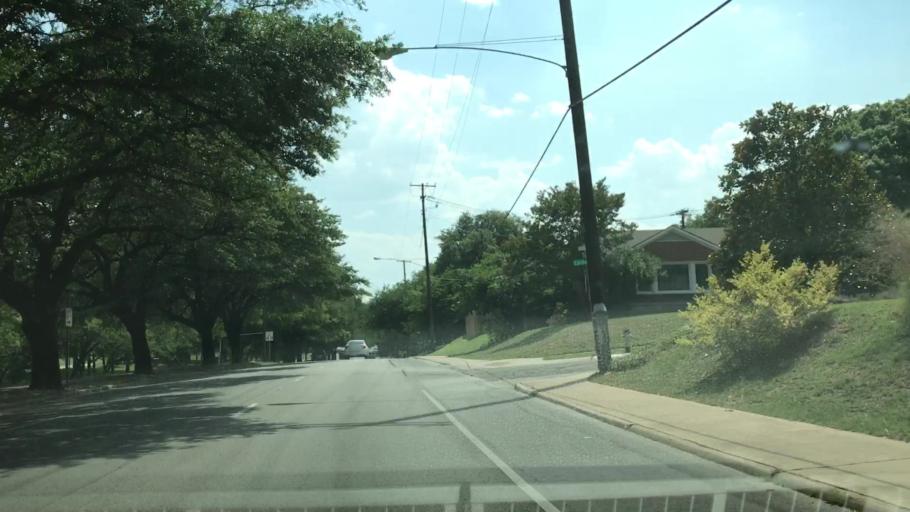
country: US
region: Texas
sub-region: Dallas County
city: Highland Park
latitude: 32.8015
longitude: -96.7390
